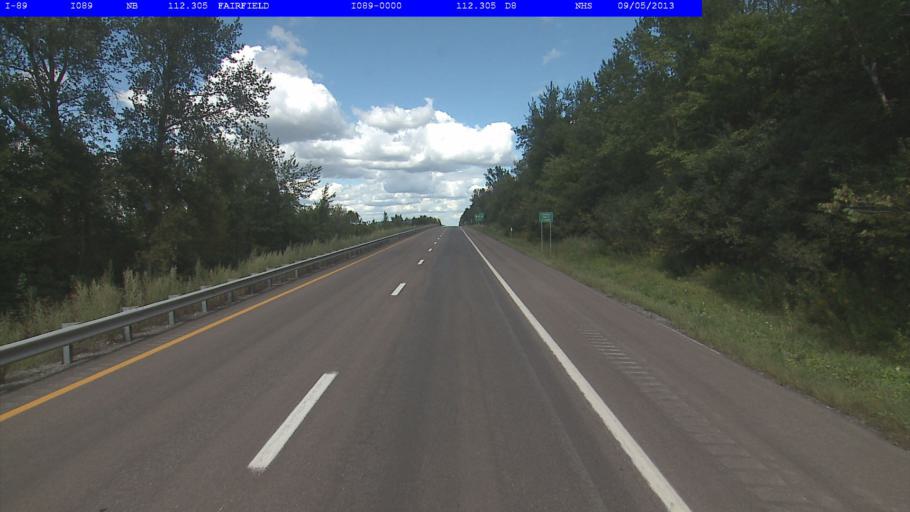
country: US
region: Vermont
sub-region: Franklin County
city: Saint Albans
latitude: 44.7742
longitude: -73.0744
